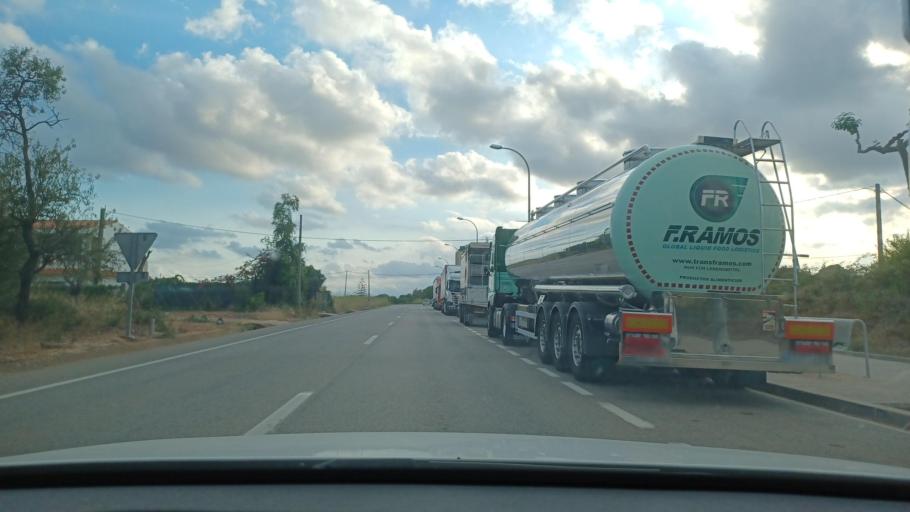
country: ES
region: Catalonia
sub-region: Provincia de Tarragona
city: Alcanar
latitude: 40.5409
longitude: 0.4851
